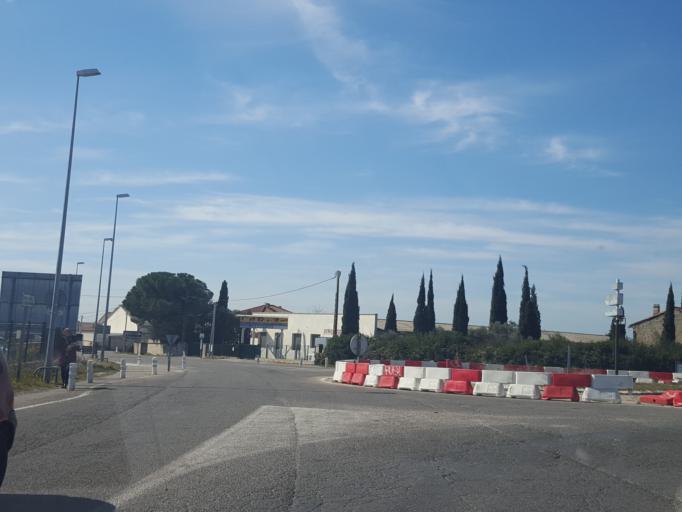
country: FR
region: Provence-Alpes-Cote d'Azur
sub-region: Departement du Vaucluse
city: Carpentras
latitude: 44.0415
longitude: 5.0413
